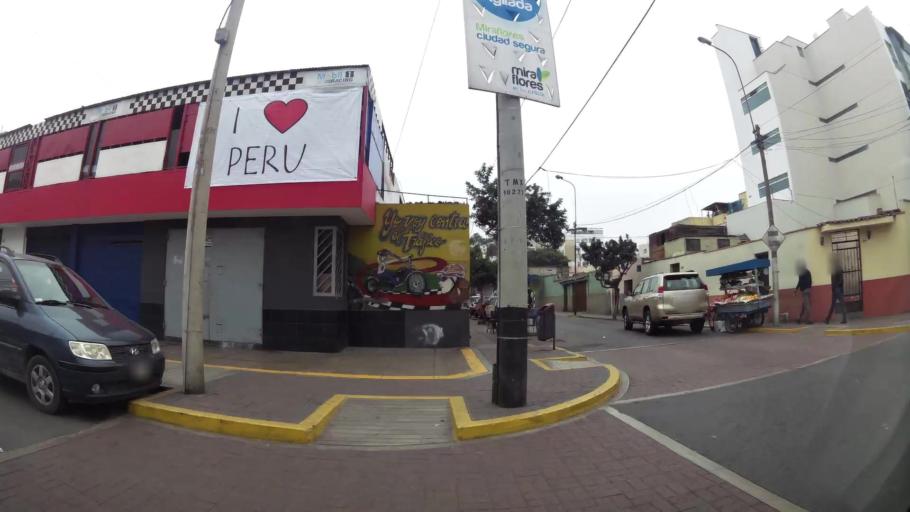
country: PE
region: Lima
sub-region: Lima
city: San Isidro
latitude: -12.1158
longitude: -77.0444
